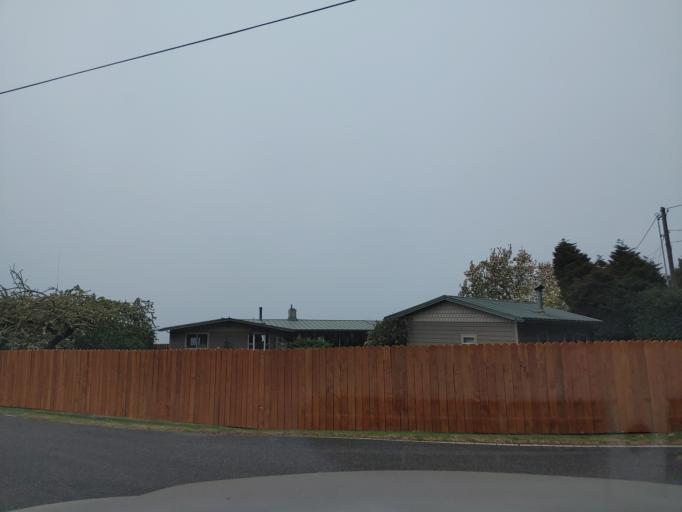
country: US
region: Oregon
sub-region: Coos County
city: Lakeside
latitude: 43.6676
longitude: -124.1937
